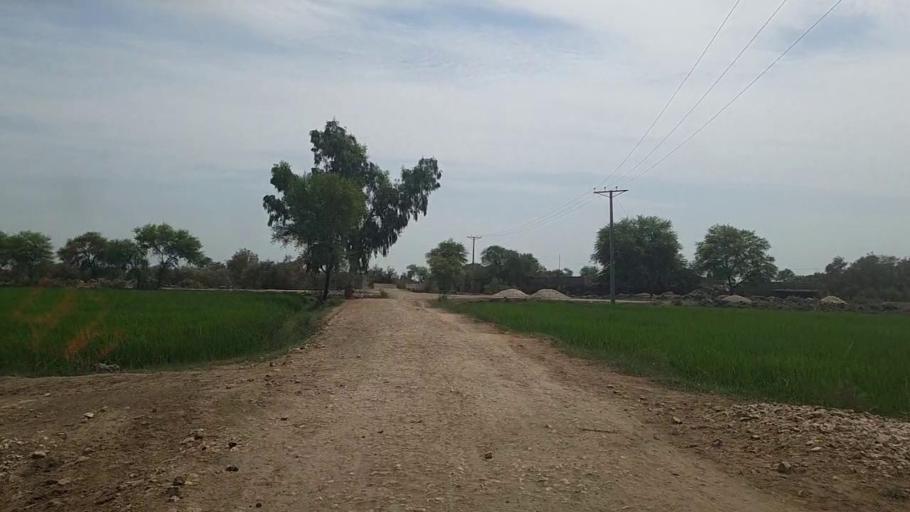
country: PK
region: Sindh
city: Thul
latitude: 28.2530
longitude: 68.6987
